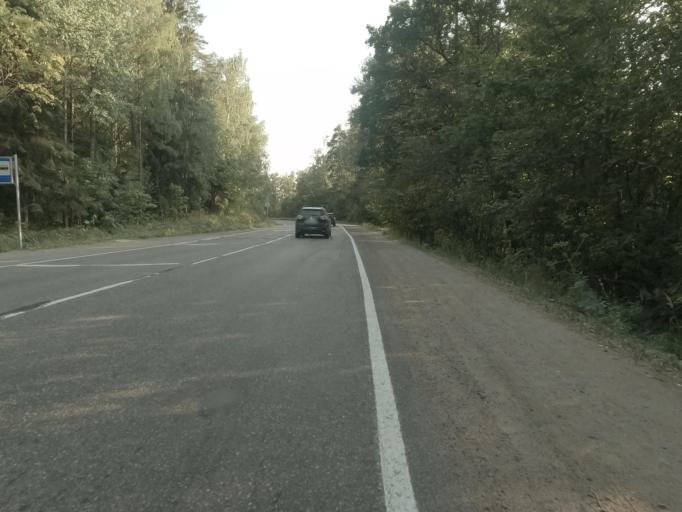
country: RU
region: Leningrad
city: Vyborg
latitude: 60.7384
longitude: 28.7597
